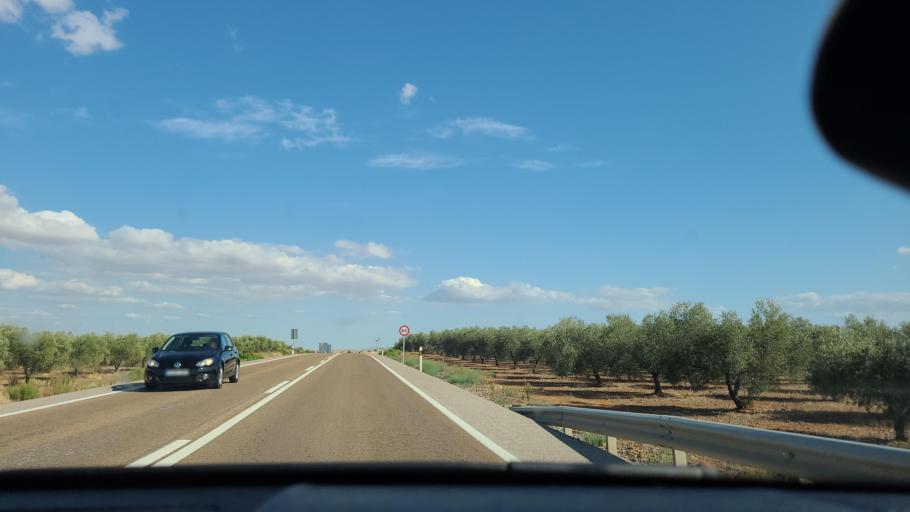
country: ES
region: Extremadura
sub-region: Provincia de Badajoz
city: Usagre
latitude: 38.3422
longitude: -6.1658
